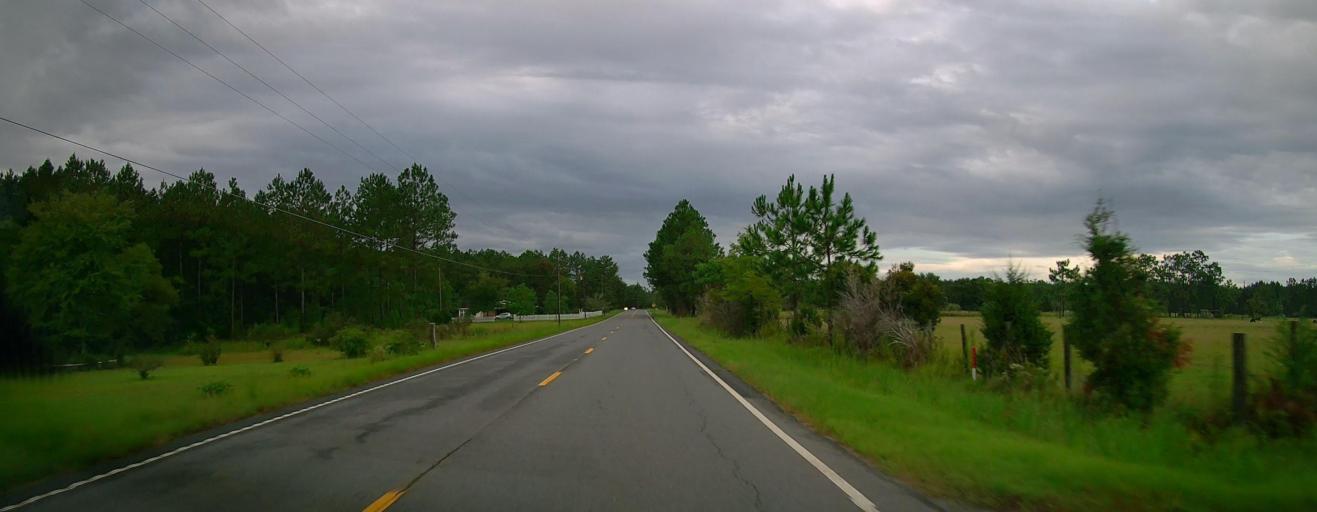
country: US
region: Georgia
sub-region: Ware County
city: Deenwood
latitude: 31.2823
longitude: -82.4295
